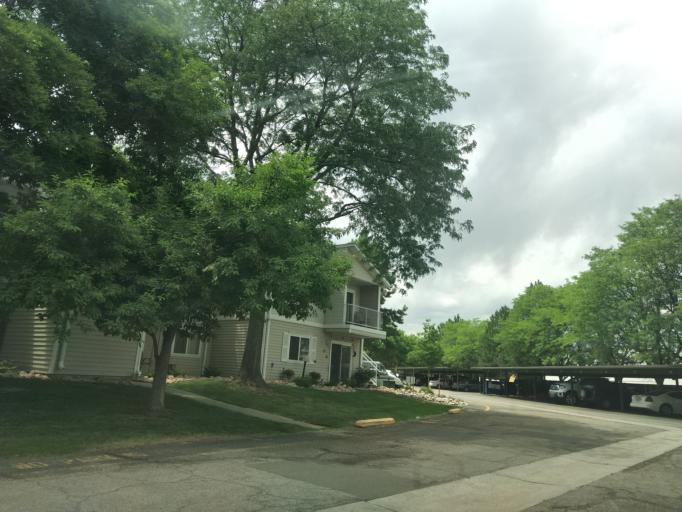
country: US
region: Colorado
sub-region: Jefferson County
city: Lakewood
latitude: 39.6894
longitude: -105.1194
